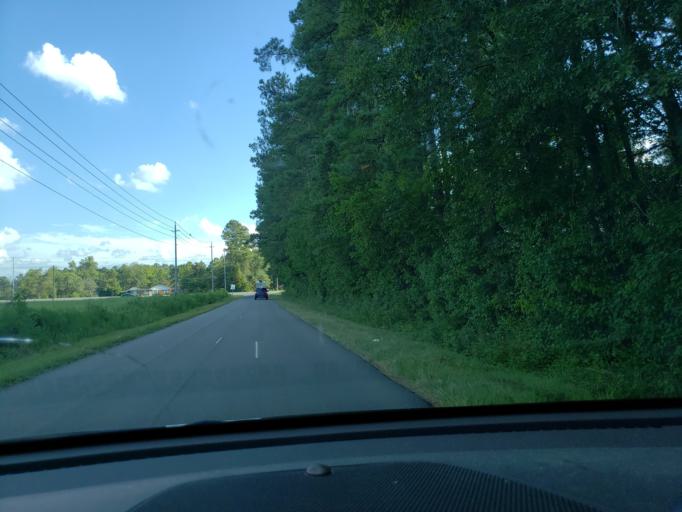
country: US
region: North Carolina
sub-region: Columbus County
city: Tabor City
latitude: 34.1608
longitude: -78.8513
